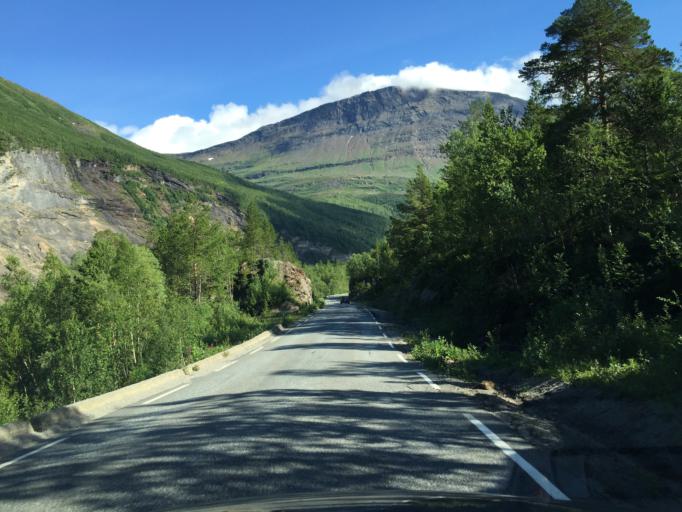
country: NO
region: Nordland
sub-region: Saltdal
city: Rognan
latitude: 66.8206
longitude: 15.4740
